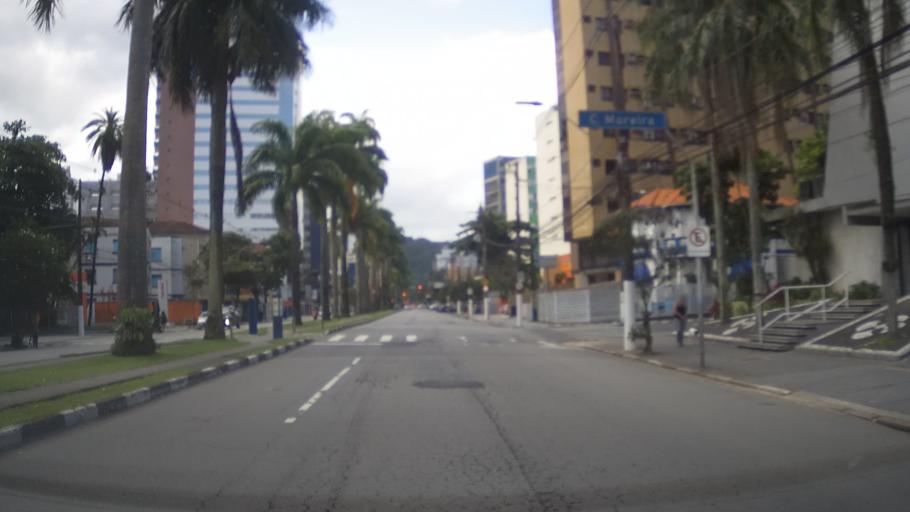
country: BR
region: Sao Paulo
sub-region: Santos
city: Santos
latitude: -23.9555
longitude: -46.3314
